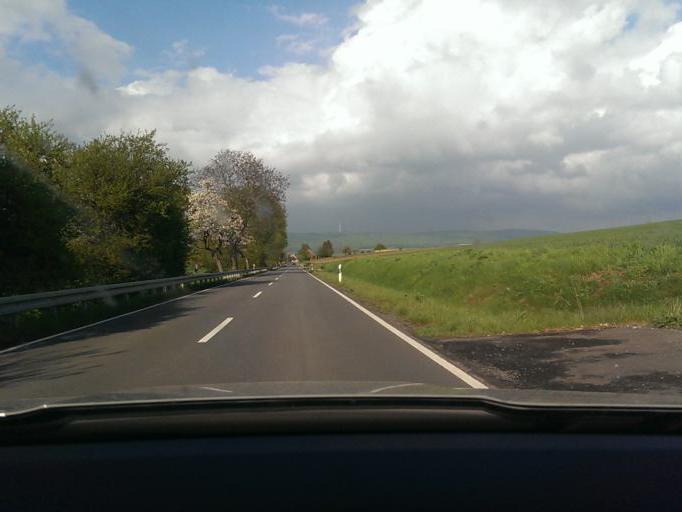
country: DE
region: Lower Saxony
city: Pohle
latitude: 52.2566
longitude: 9.3253
